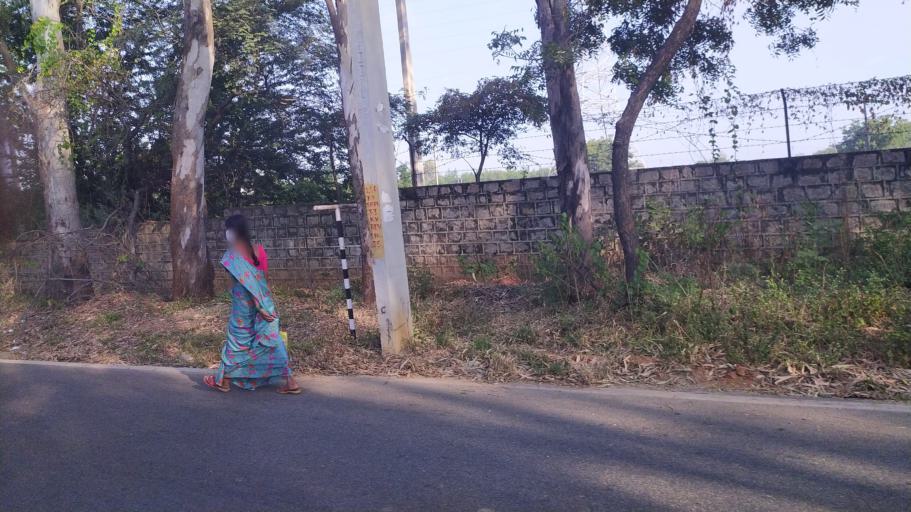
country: IN
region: Telangana
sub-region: Hyderabad
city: Hyderabad
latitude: 17.3297
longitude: 78.4123
